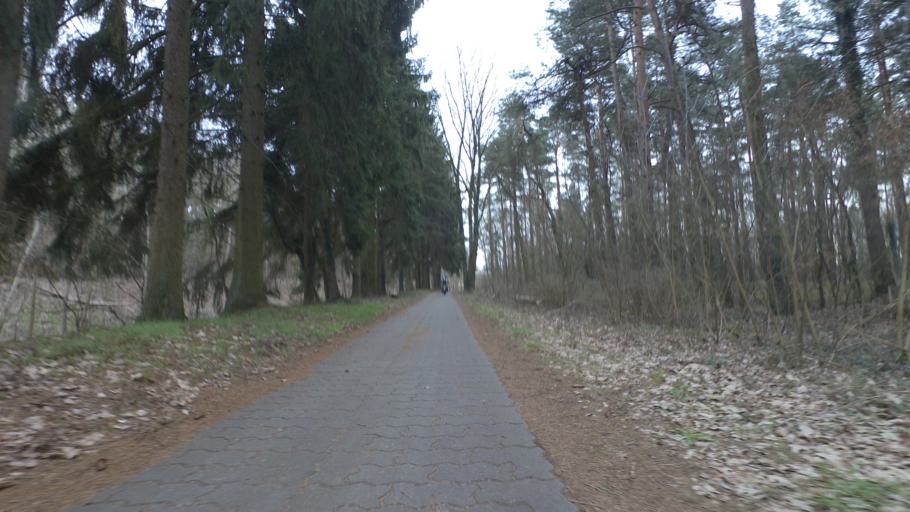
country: DE
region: Brandenburg
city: Lindow
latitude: 52.9805
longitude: 12.9794
